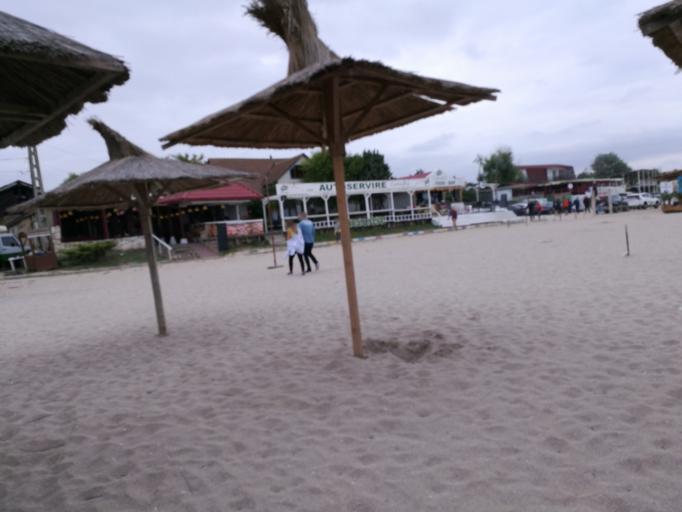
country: RO
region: Constanta
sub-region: Municipiul Mangalia
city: Mangalia
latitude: 43.7544
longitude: 28.5745
